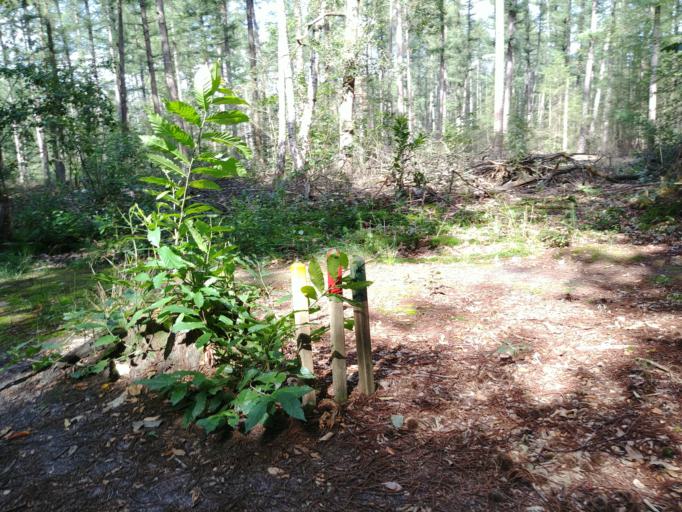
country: NL
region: Utrecht
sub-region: Gemeente Utrechtse Heuvelrug
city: Maarn
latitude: 52.0524
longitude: 5.3582
